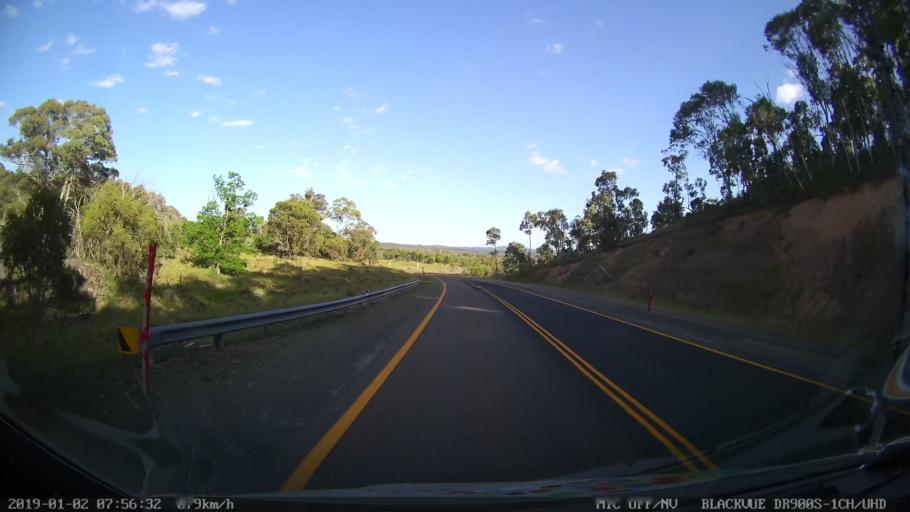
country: AU
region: New South Wales
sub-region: Tumut Shire
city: Tumut
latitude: -35.6697
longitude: 148.4845
